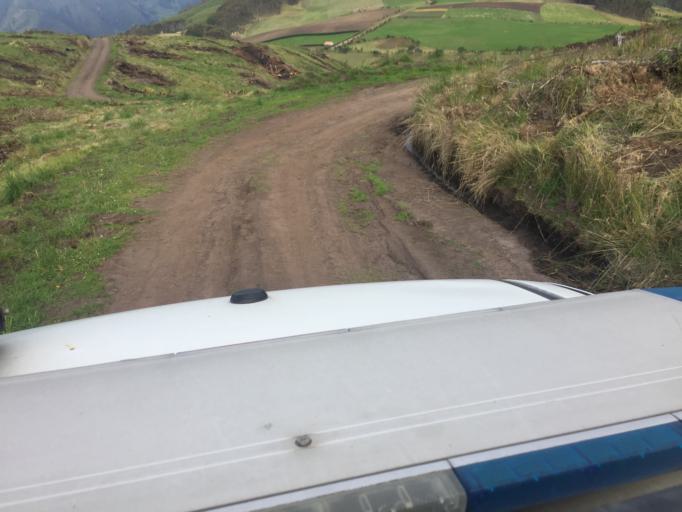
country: EC
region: Imbabura
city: Ibarra
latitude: 0.2251
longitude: -78.1233
